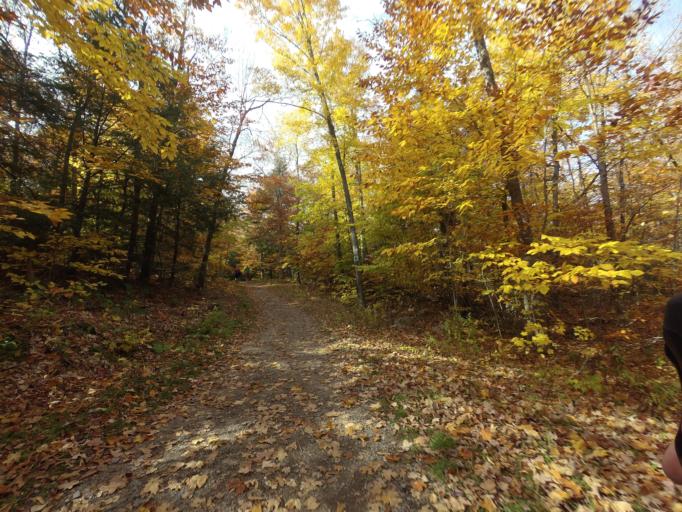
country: CA
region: Quebec
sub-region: Outaouais
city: Gatineau
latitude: 45.4998
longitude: -75.8470
